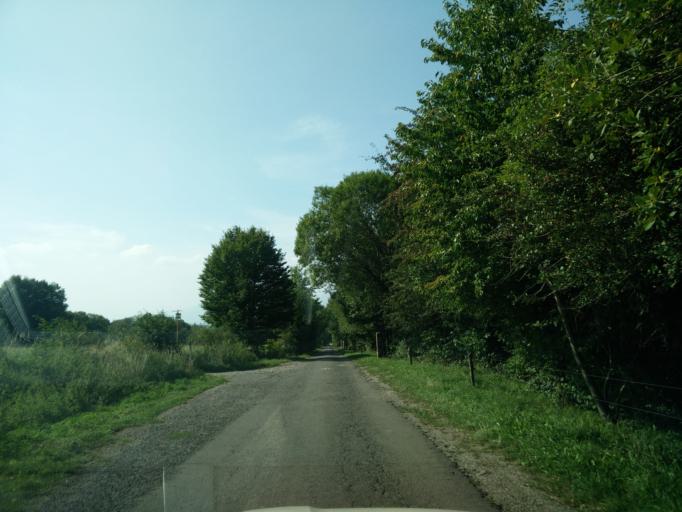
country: SK
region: Nitriansky
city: Novaky
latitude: 48.6786
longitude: 18.6164
